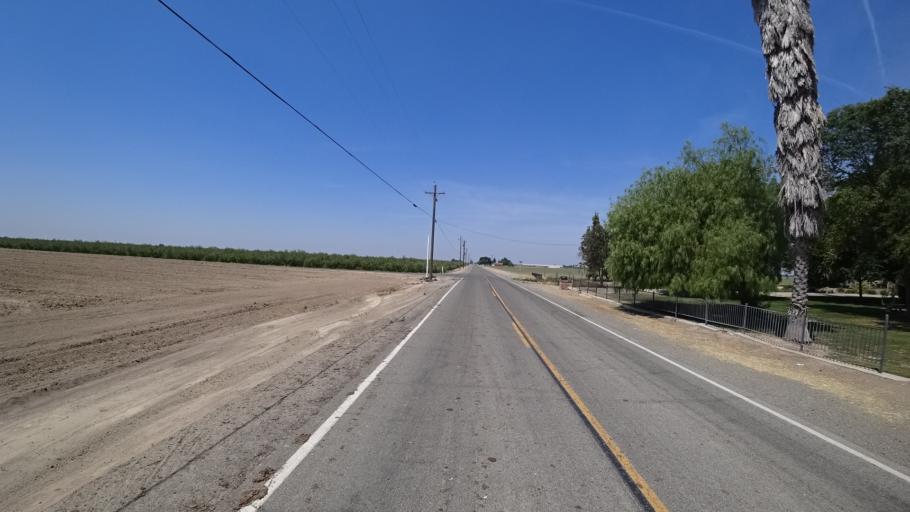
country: US
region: California
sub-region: Fresno County
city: Kingsburg
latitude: 36.4014
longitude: -119.5462
